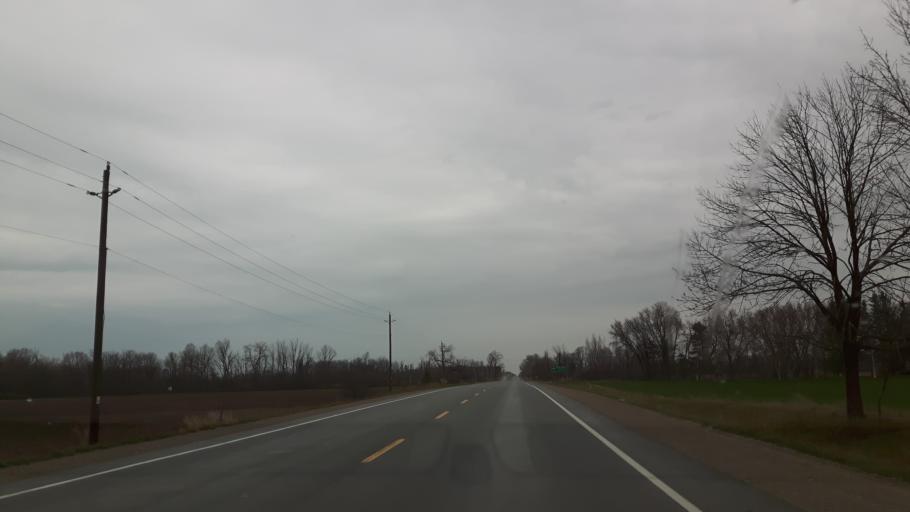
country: CA
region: Ontario
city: Goderich
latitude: 43.5916
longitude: -81.7056
